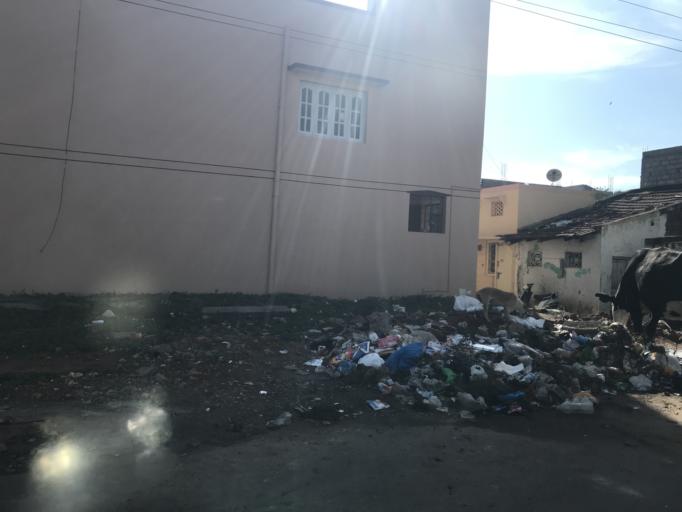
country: IN
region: Karnataka
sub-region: Mysore
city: Mysore
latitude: 12.2904
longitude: 76.6414
